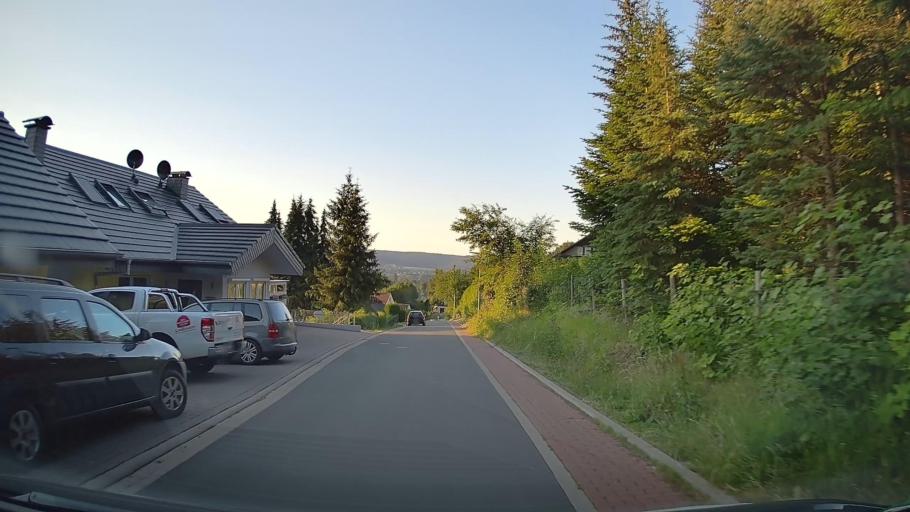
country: DE
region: North Rhine-Westphalia
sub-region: Regierungsbezirk Detmold
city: Lugde
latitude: 51.9532
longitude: 9.2484
